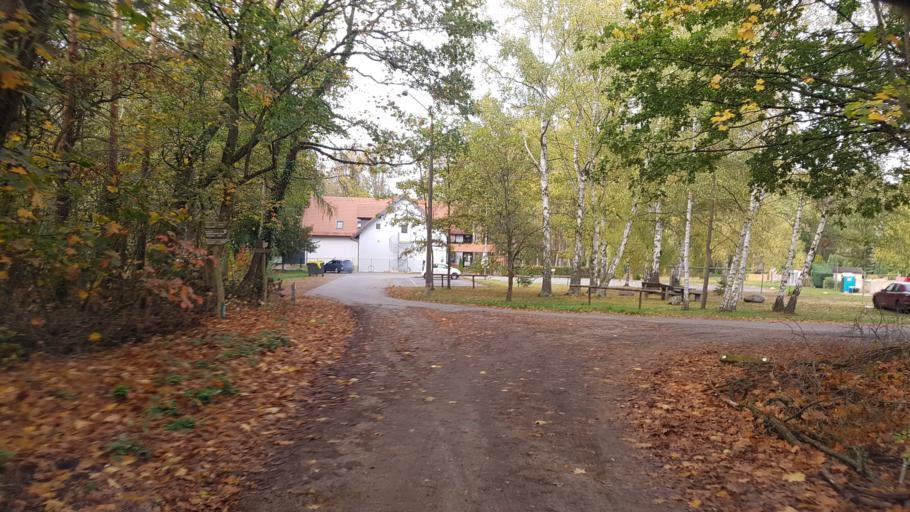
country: DE
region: Brandenburg
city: Doberlug-Kirchhain
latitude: 51.6355
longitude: 13.5332
